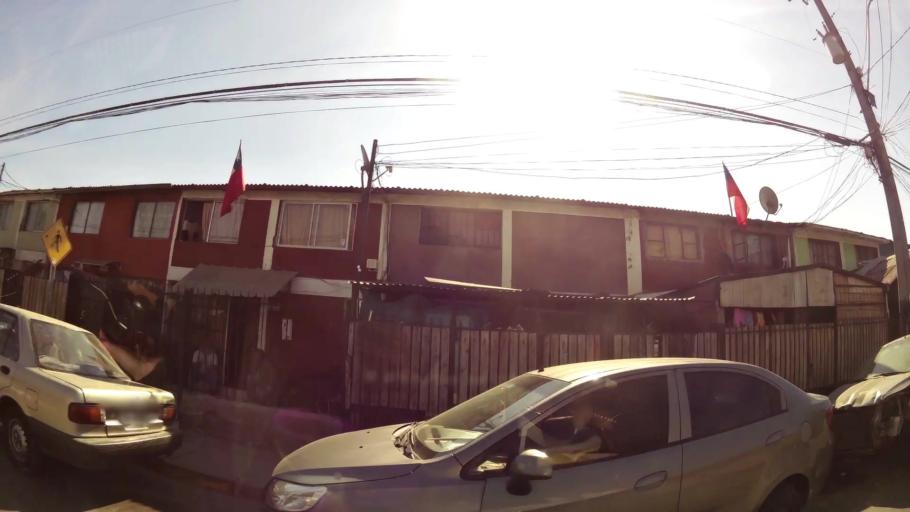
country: CL
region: Santiago Metropolitan
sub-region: Provincia de Santiago
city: Villa Presidente Frei, Nunoa, Santiago, Chile
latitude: -33.4804
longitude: -70.5715
